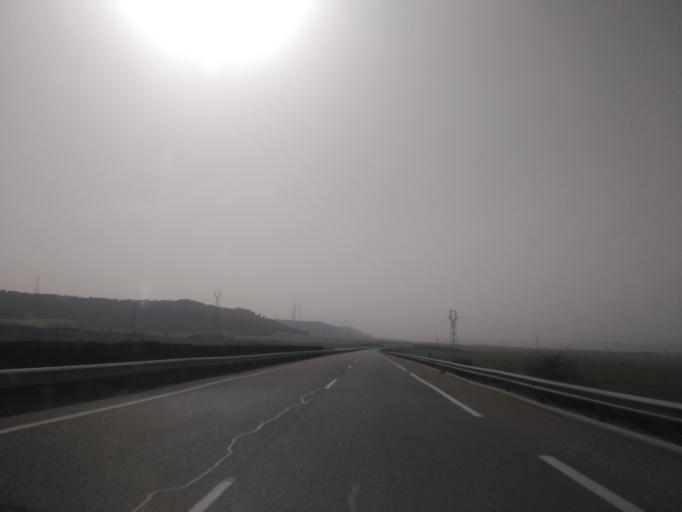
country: ES
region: Castille and Leon
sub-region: Provincia de Palencia
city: Villalobon
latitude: 42.0312
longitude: -4.4910
